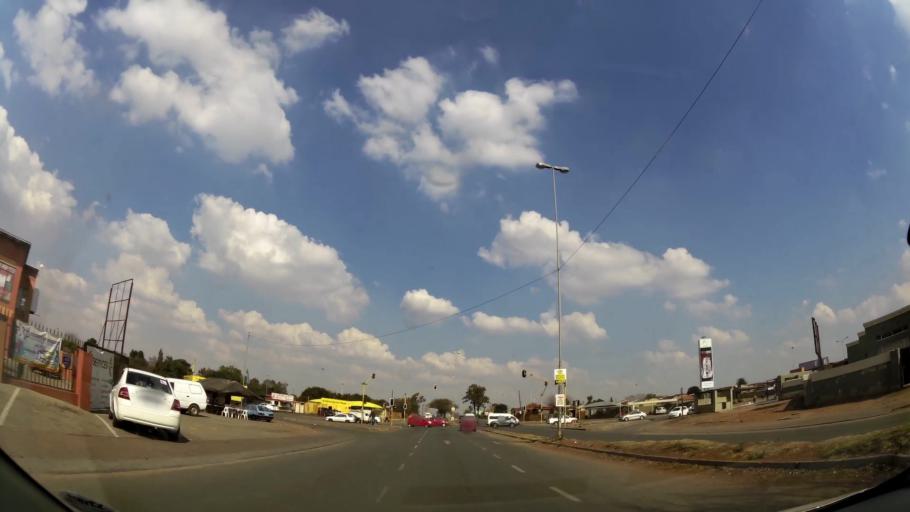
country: ZA
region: Gauteng
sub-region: Ekurhuleni Metropolitan Municipality
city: Germiston
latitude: -26.3437
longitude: 28.1618
